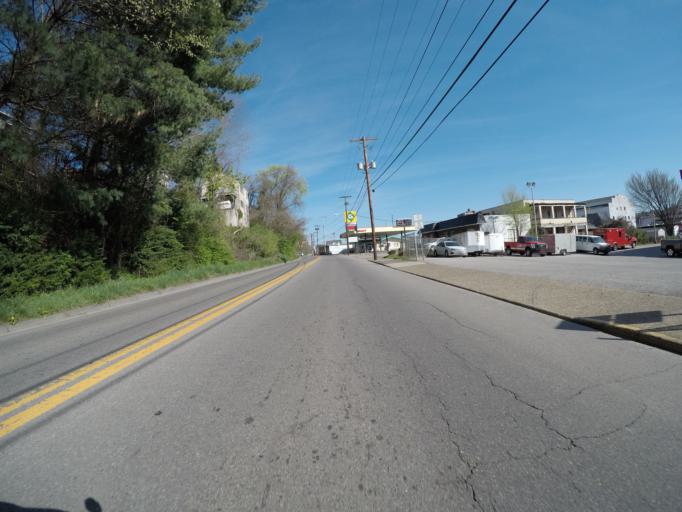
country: US
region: West Virginia
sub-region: Kanawha County
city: Charleston
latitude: 38.3675
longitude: -81.6520
